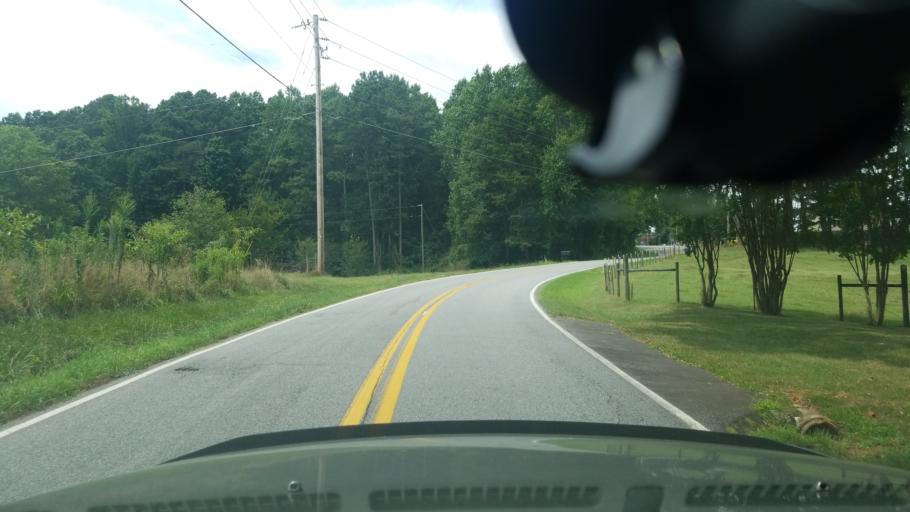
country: US
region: Georgia
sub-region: Forsyth County
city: Cumming
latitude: 34.2252
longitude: -84.2127
